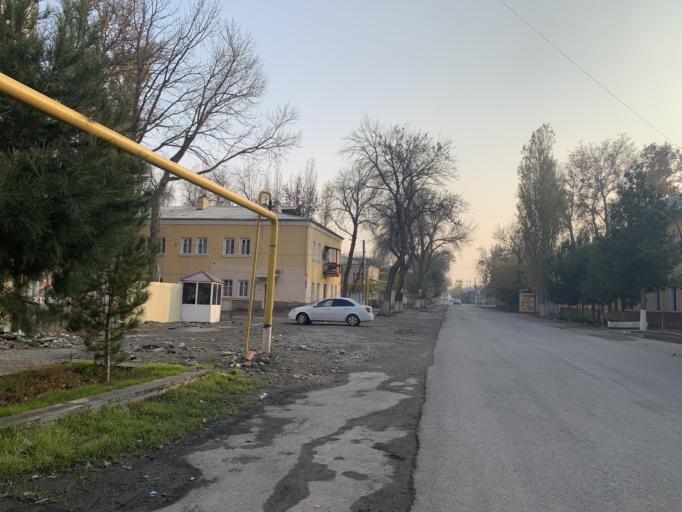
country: UZ
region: Fergana
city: Qo`qon
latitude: 40.5239
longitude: 70.9383
